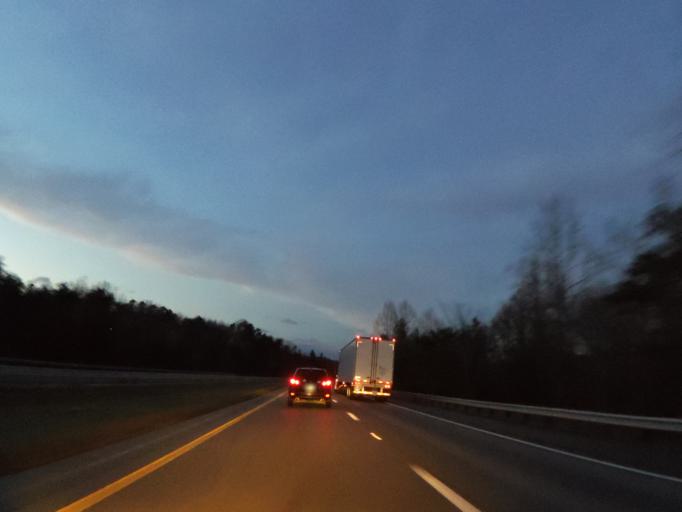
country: US
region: Kentucky
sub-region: Whitley County
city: Corbin
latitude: 36.8799
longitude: -84.1500
